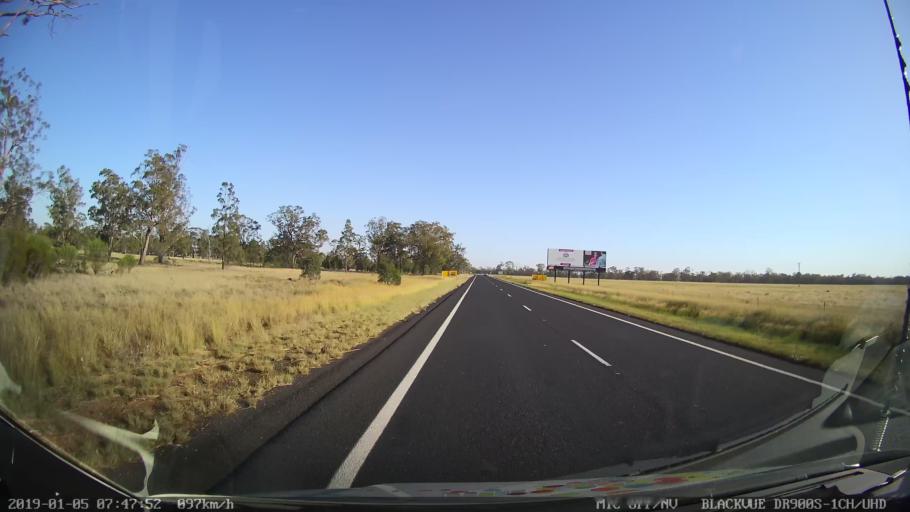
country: AU
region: New South Wales
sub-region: Gilgandra
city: Gilgandra
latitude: -31.8246
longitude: 148.6386
